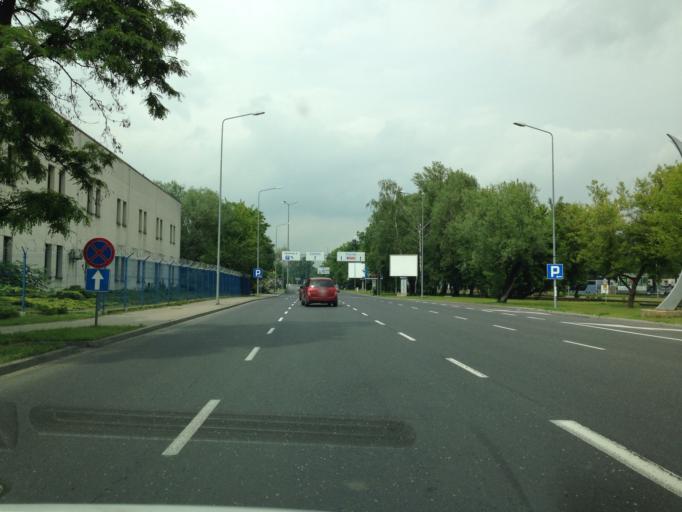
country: PL
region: Masovian Voivodeship
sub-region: Warszawa
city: Wlochy
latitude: 52.1700
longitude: 20.9780
